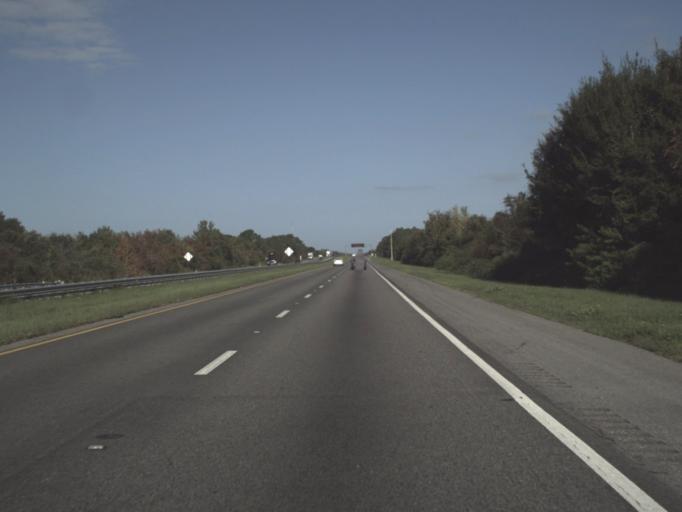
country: US
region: Florida
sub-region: Osceola County
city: Saint Cloud
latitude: 28.0656
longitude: -81.2385
